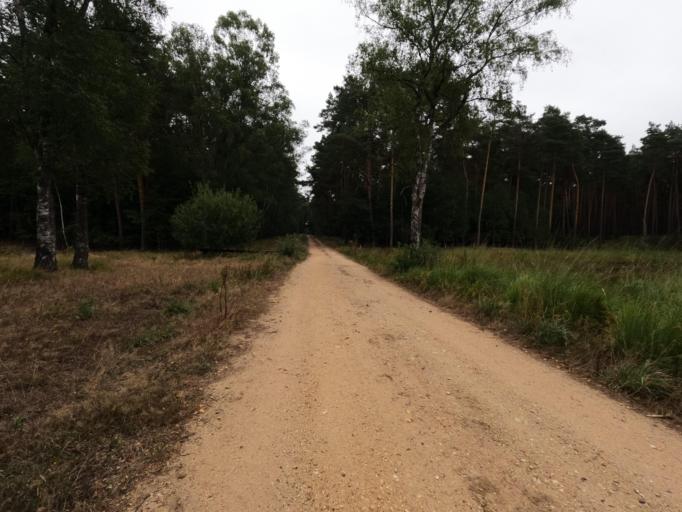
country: DE
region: North Rhine-Westphalia
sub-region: Regierungsbezirk Dusseldorf
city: Niederkruchten
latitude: 51.1722
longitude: 6.1664
